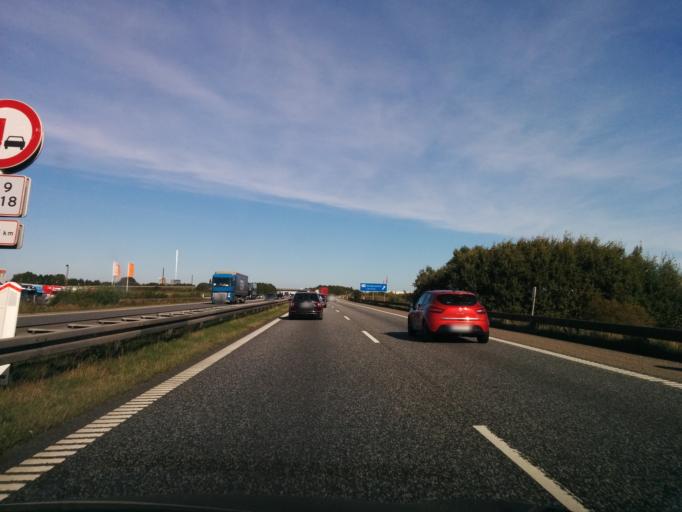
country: DK
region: Central Jutland
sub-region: Hedensted Kommune
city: Hedensted
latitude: 55.7859
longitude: 9.6656
